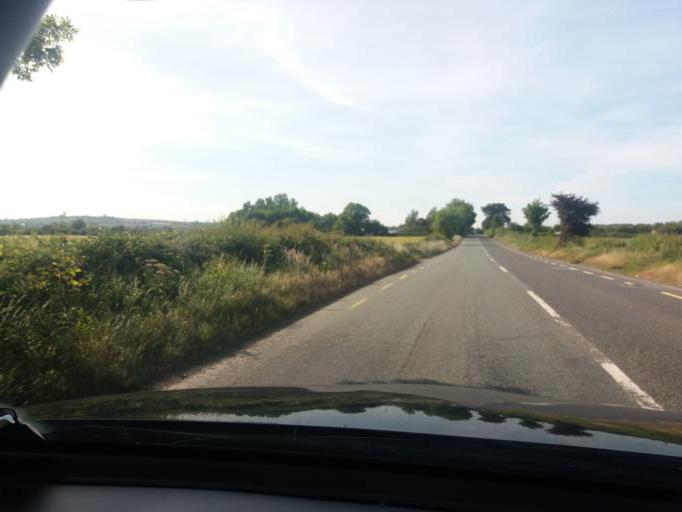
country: IE
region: Leinster
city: Lusk
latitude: 53.5401
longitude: -6.2011
